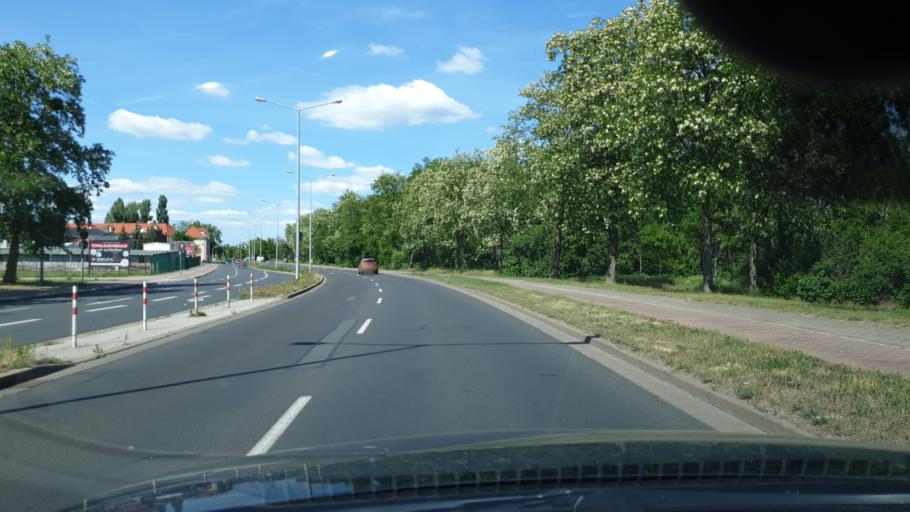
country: DE
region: Saxony-Anhalt
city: Dessau
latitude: 51.8151
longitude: 12.2501
